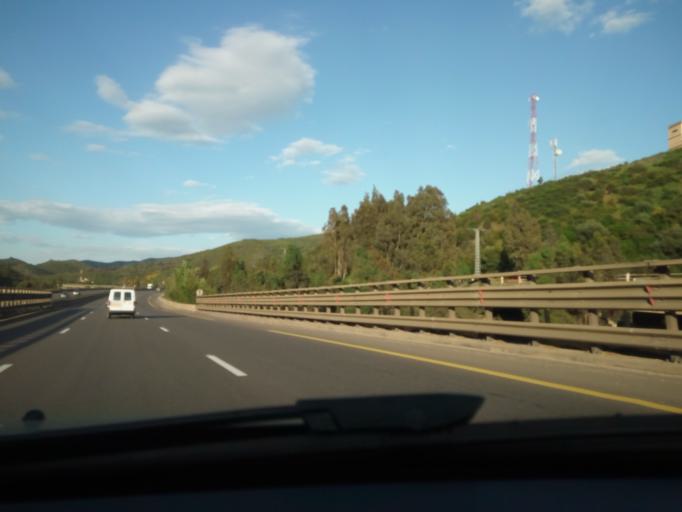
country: DZ
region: Tipaza
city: El Affroun
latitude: 36.3945
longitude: 2.5300
